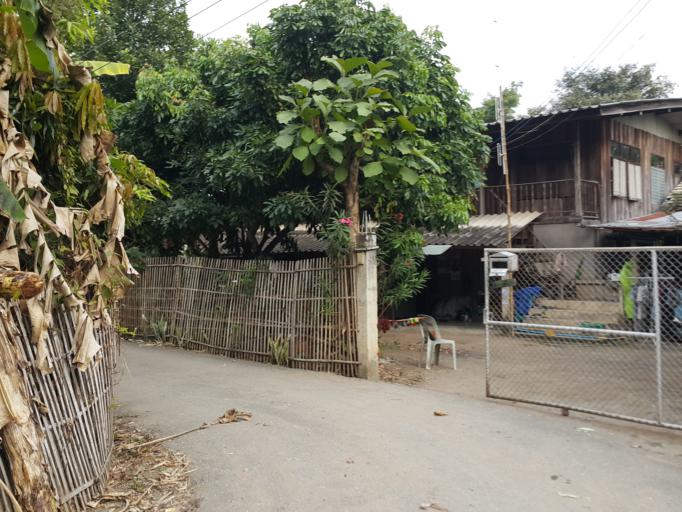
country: TH
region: Chiang Mai
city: San Kamphaeng
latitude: 18.8254
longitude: 99.1452
